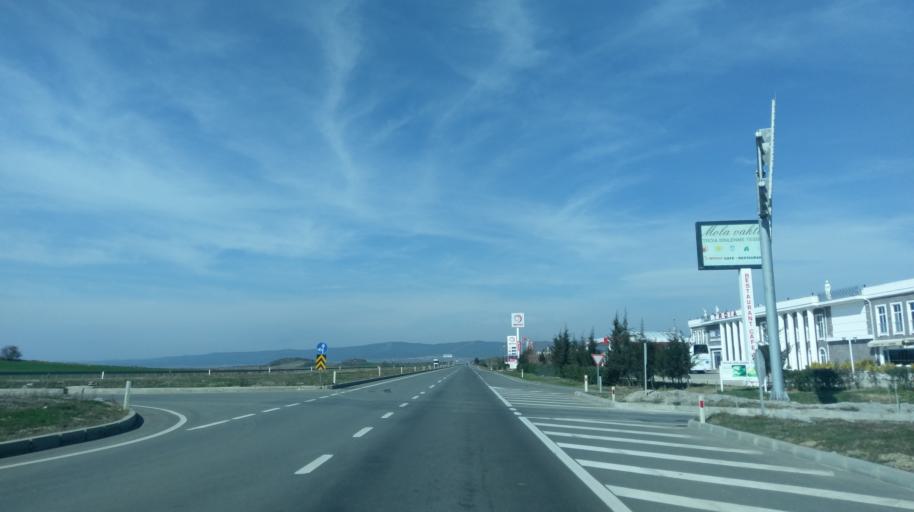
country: TR
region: Canakkale
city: Evrese
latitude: 40.6392
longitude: 26.8598
